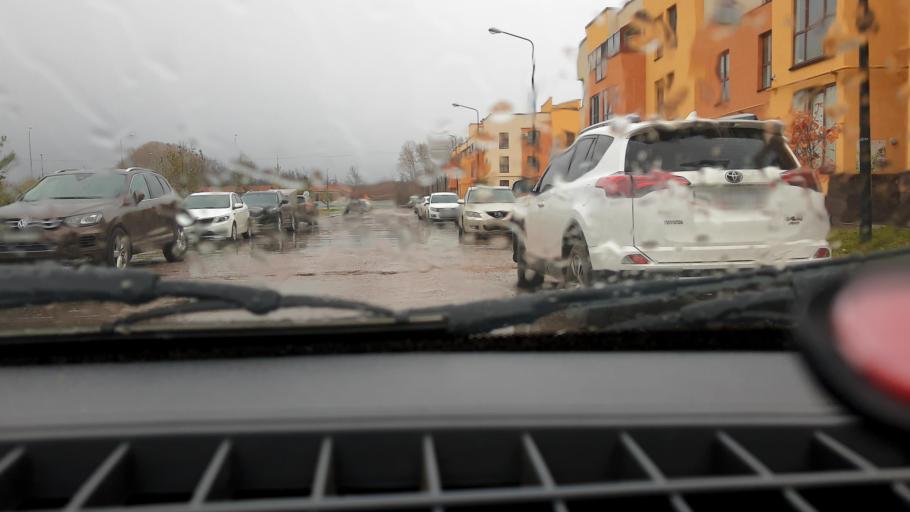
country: RU
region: Bashkortostan
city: Ufa
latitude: 54.7967
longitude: 55.9567
